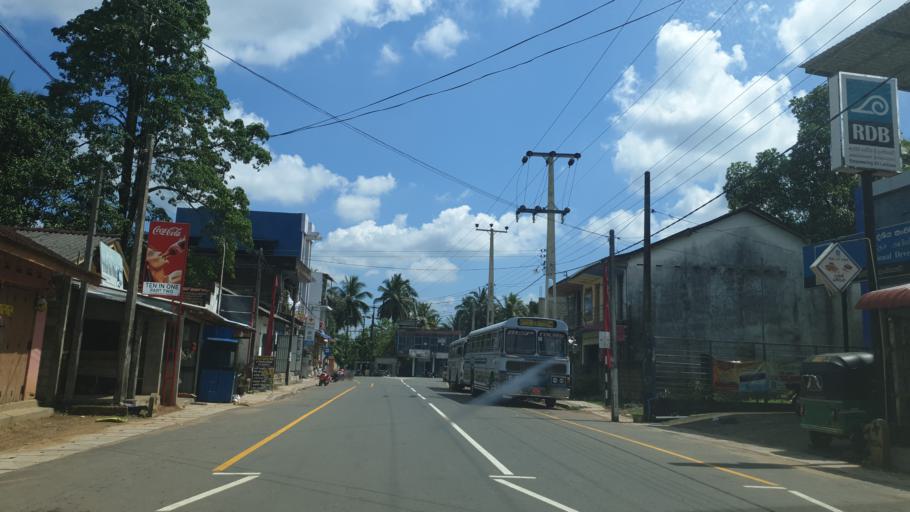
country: LK
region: Western
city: Kalutara
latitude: 6.6632
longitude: 79.9711
